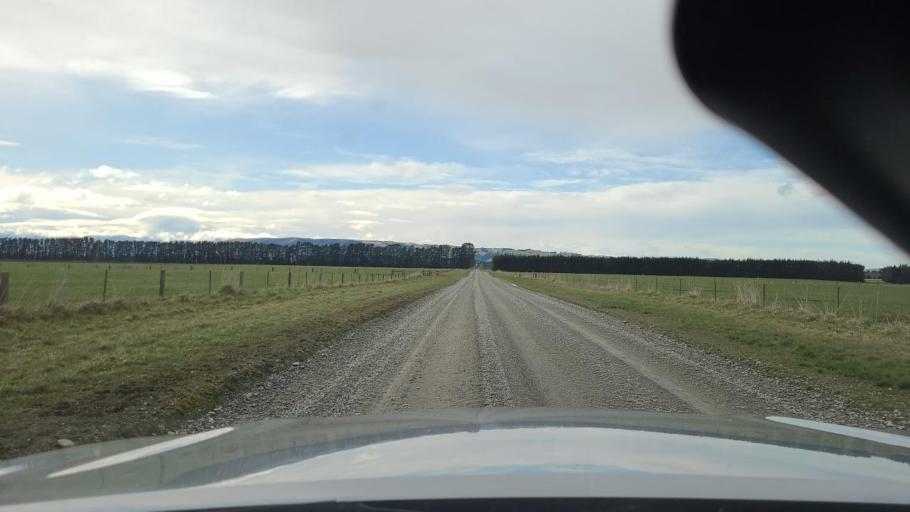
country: NZ
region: Southland
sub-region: Gore District
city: Gore
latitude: -45.7915
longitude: 168.6970
